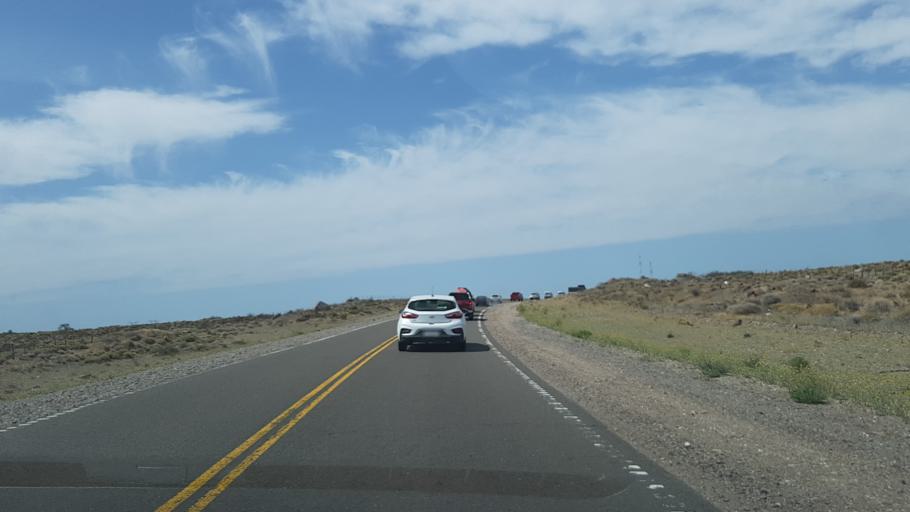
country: AR
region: Neuquen
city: Piedra del Aguila
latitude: -39.9874
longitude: -70.0397
